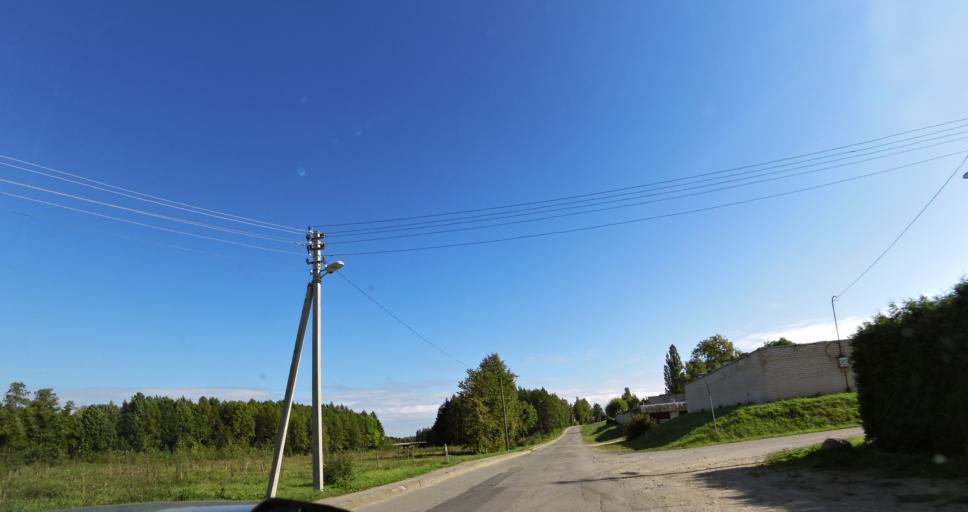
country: LT
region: Panevezys
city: Pasvalys
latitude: 56.0669
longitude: 24.4195
